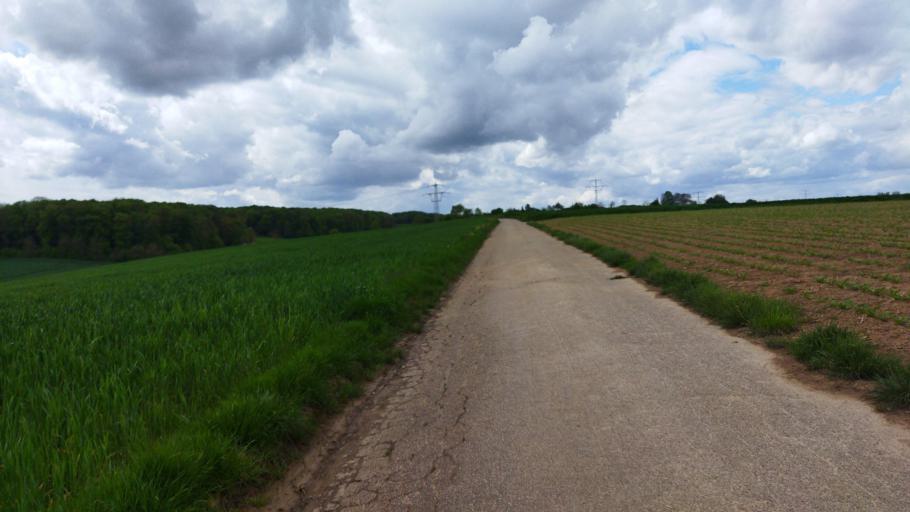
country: DE
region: Baden-Wuerttemberg
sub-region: Regierungsbezirk Stuttgart
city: Leingarten
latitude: 49.1728
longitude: 9.1200
